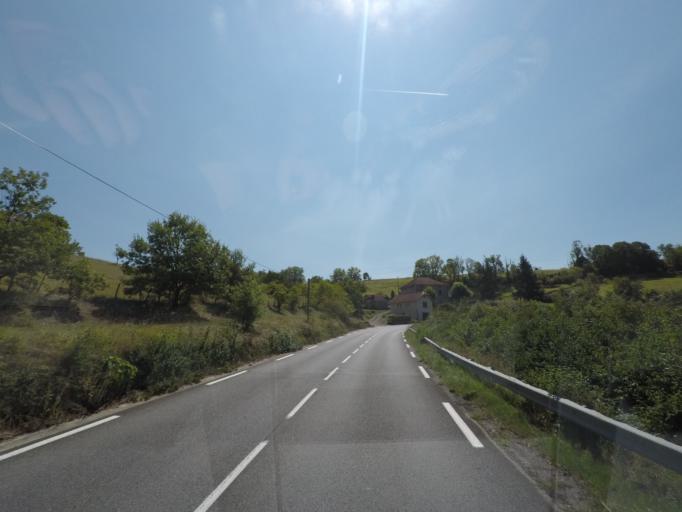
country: FR
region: Midi-Pyrenees
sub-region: Departement du Lot
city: Figeac
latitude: 44.6009
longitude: 2.0611
